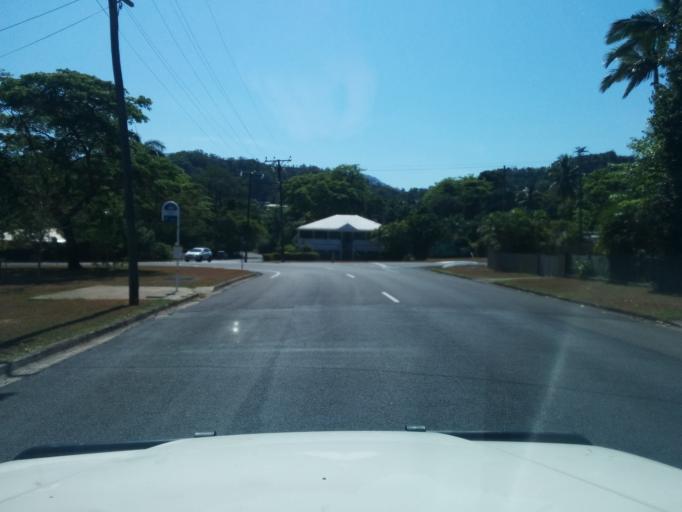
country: AU
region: Queensland
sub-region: Cairns
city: Redlynch
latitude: -16.9002
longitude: 145.7296
